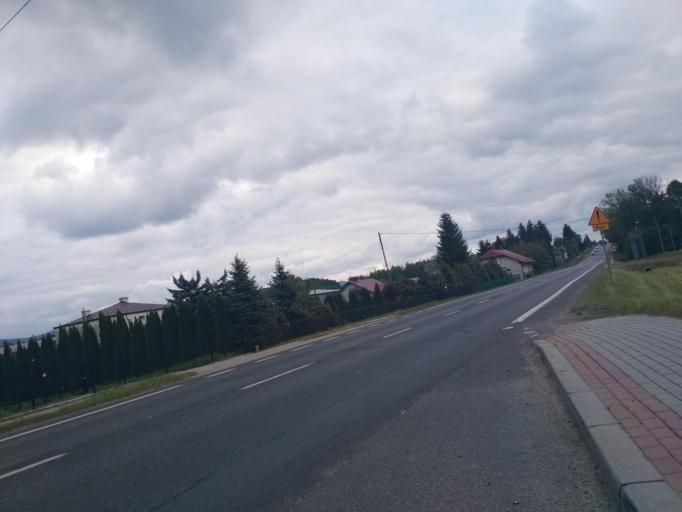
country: PL
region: Subcarpathian Voivodeship
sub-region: Powiat krosnienski
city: Odrzykon
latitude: 49.7220
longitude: 21.6989
